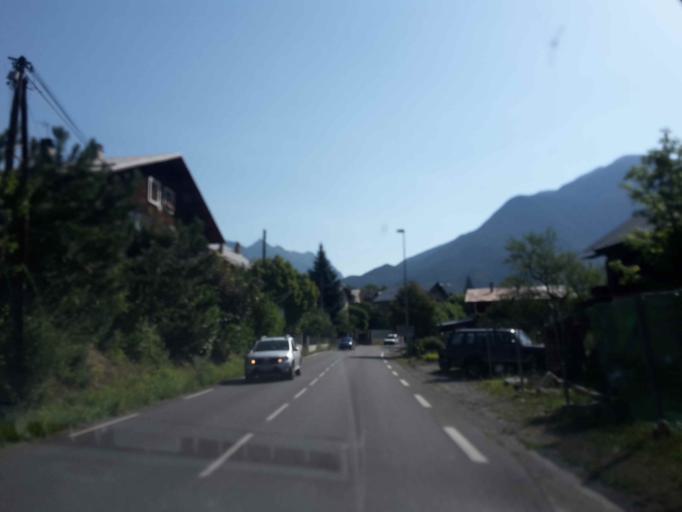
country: FR
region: Provence-Alpes-Cote d'Azur
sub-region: Departement des Hautes-Alpes
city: Guillestre
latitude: 44.6598
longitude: 6.6392
